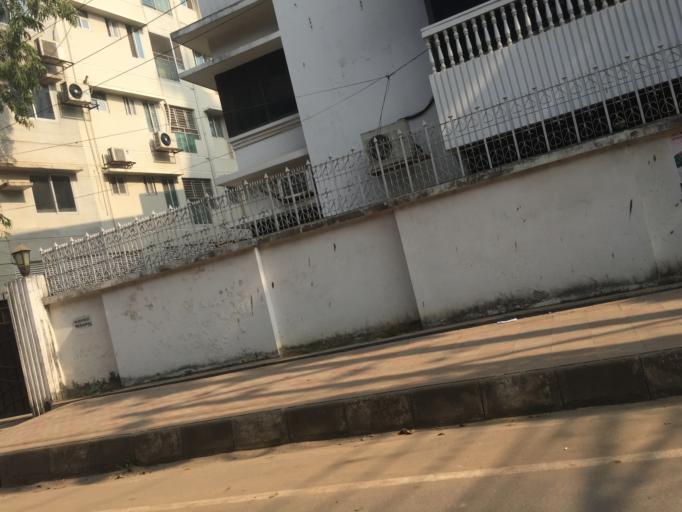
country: BD
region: Dhaka
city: Paltan
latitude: 23.7942
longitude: 90.4195
